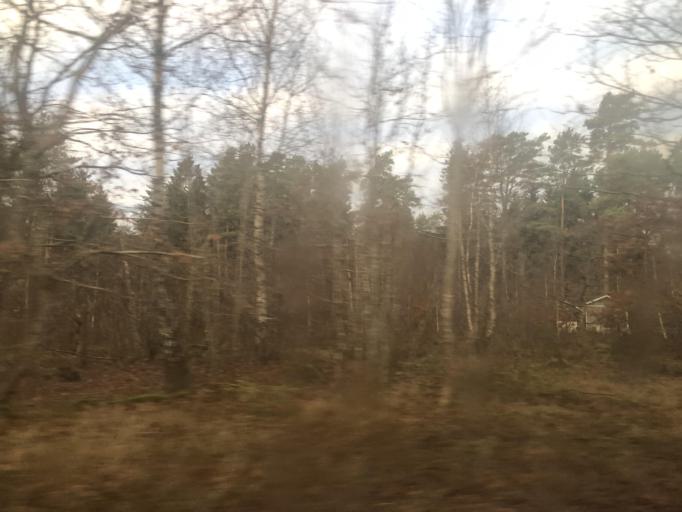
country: SE
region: Skane
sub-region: Sjobo Kommun
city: Blentarp
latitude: 55.6135
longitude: 13.5464
